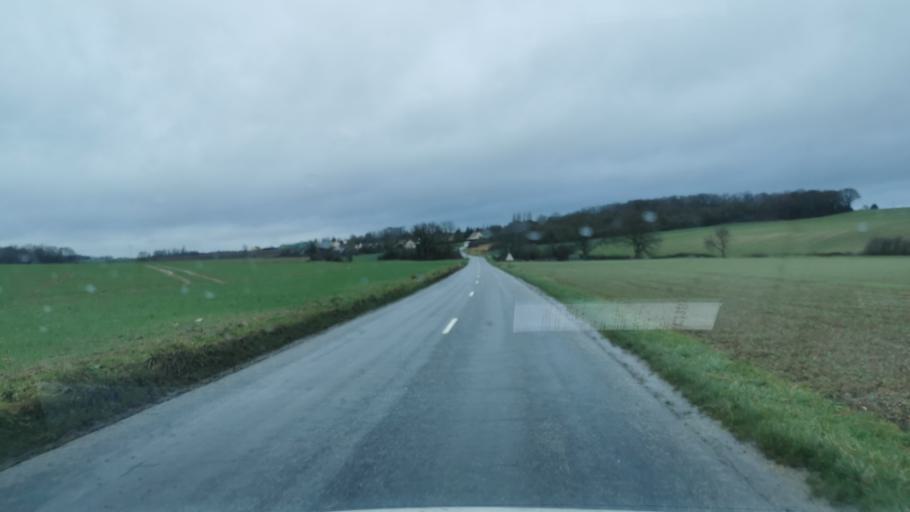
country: FR
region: Ile-de-France
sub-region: Departement des Yvelines
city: Longnes
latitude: 48.9099
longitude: 1.5890
